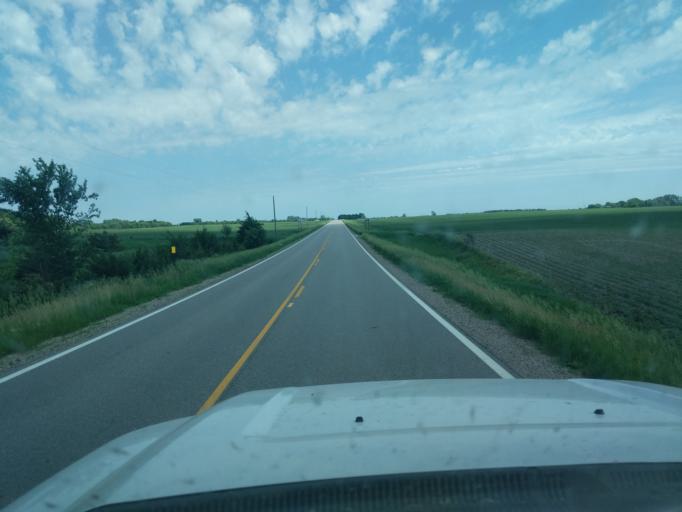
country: US
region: Minnesota
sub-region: Yellow Medicine County
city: Granite Falls
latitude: 44.7501
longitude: -95.4017
